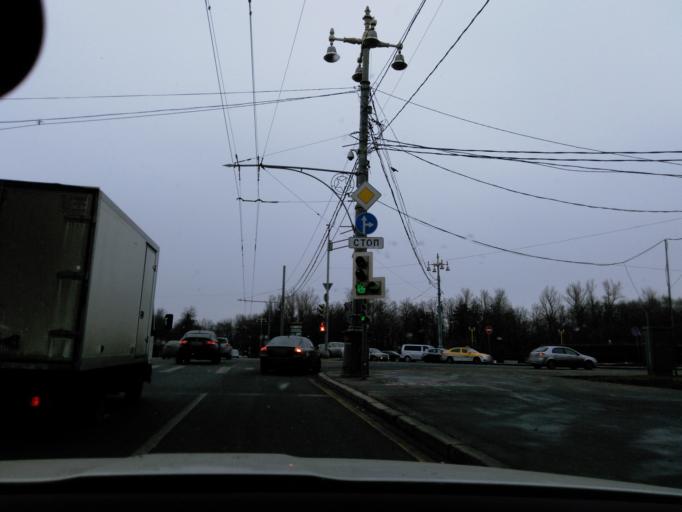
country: RU
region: Moscow
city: Vorob'yovo
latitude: 55.7095
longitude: 37.5405
